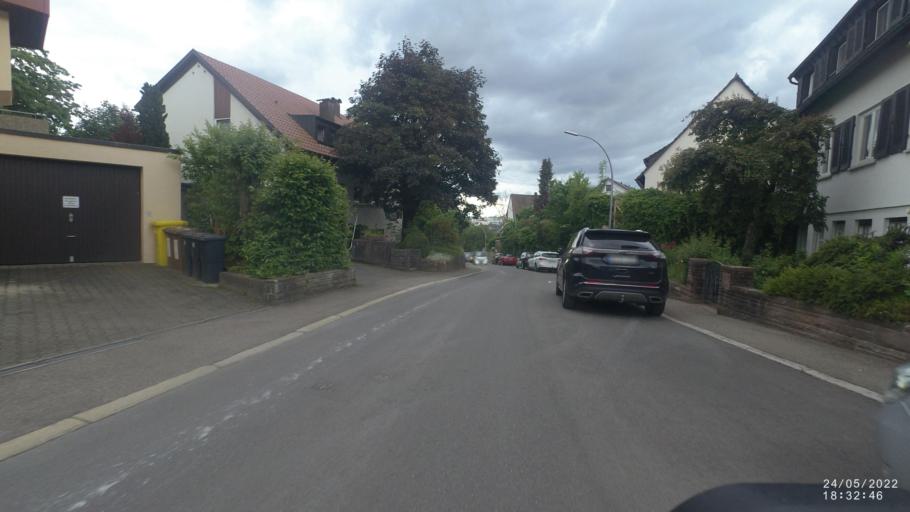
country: DE
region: Baden-Wuerttemberg
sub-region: Regierungsbezirk Stuttgart
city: Fellbach
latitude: 48.8351
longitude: 9.2668
